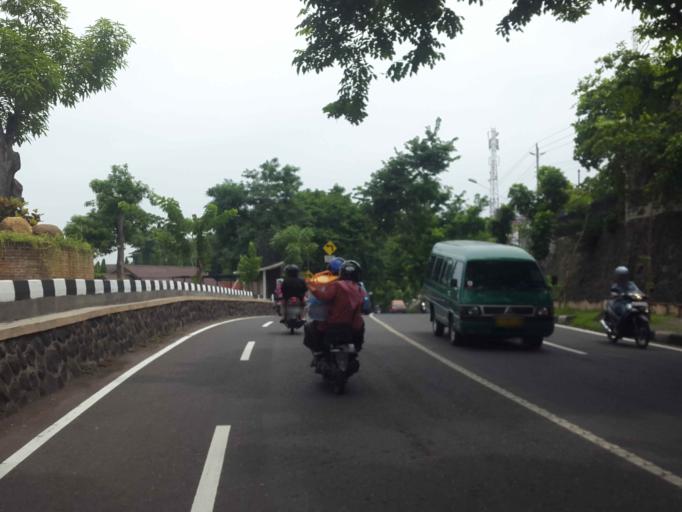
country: ID
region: Central Java
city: Semarang
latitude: -7.0162
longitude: 110.4293
